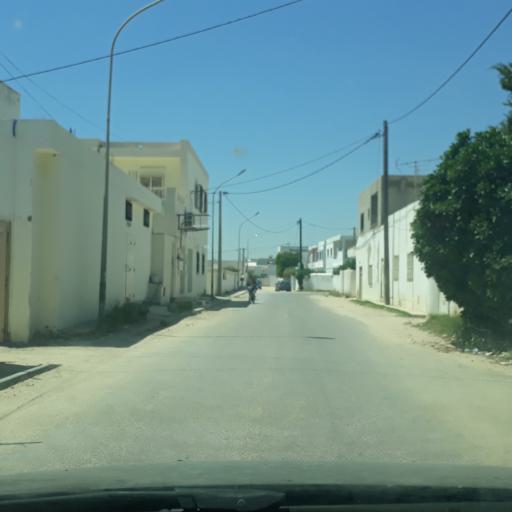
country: TN
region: Safaqis
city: Al Qarmadah
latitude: 34.8124
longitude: 10.7601
